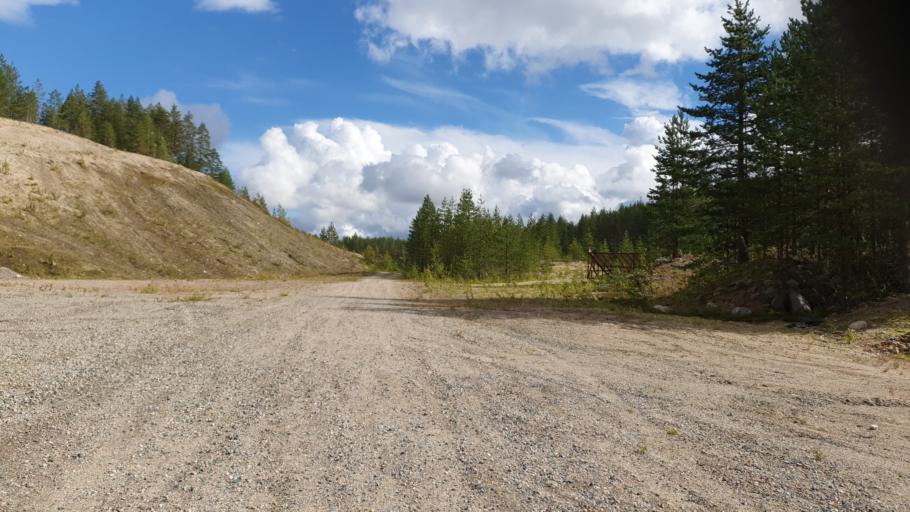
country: FI
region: Kainuu
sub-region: Kehys-Kainuu
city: Kuhmo
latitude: 64.1529
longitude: 29.3805
